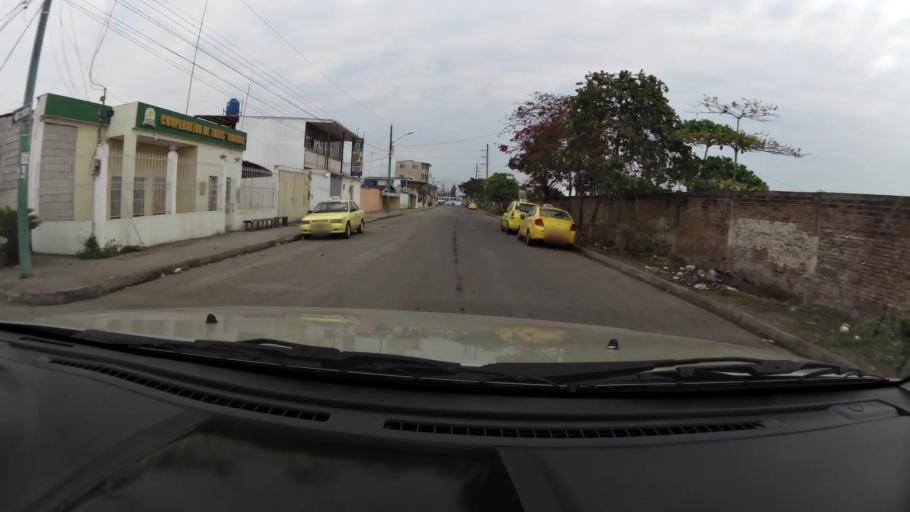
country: EC
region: El Oro
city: Machala
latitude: -3.2665
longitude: -79.9416
